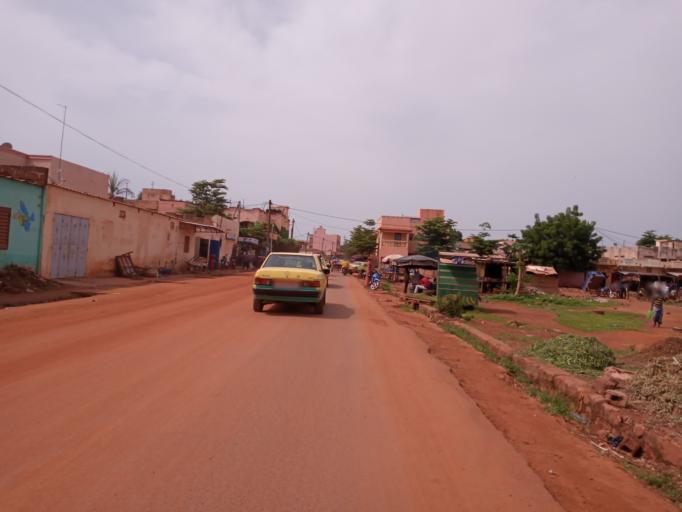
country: ML
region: Bamako
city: Bamako
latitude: 12.5616
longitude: -7.9902
